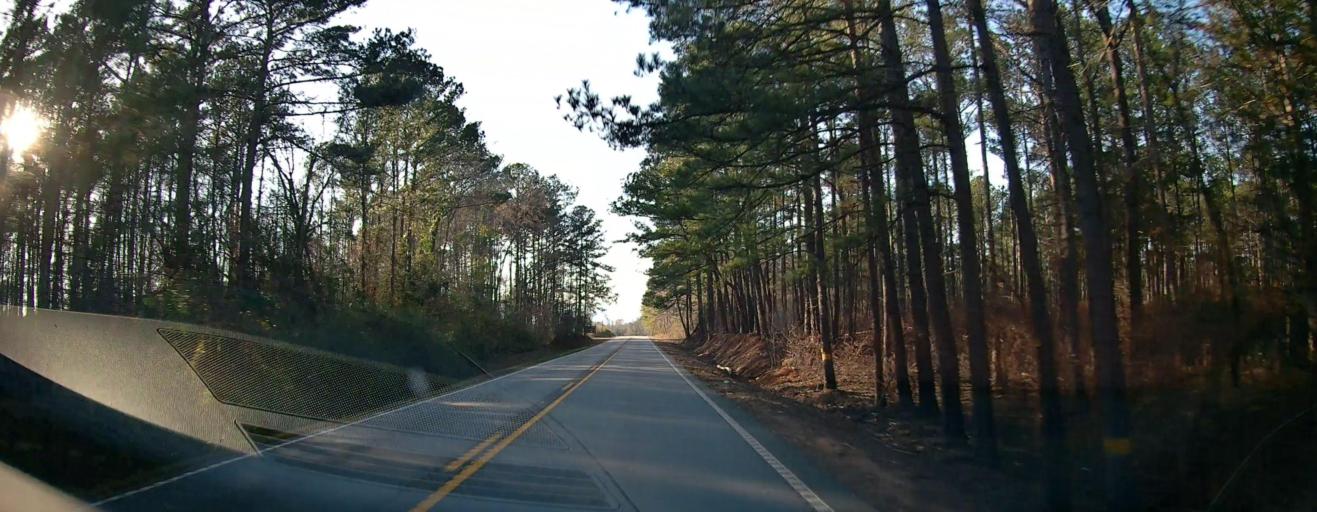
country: US
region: Alabama
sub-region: Chambers County
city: Valley
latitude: 32.7755
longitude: -85.0840
